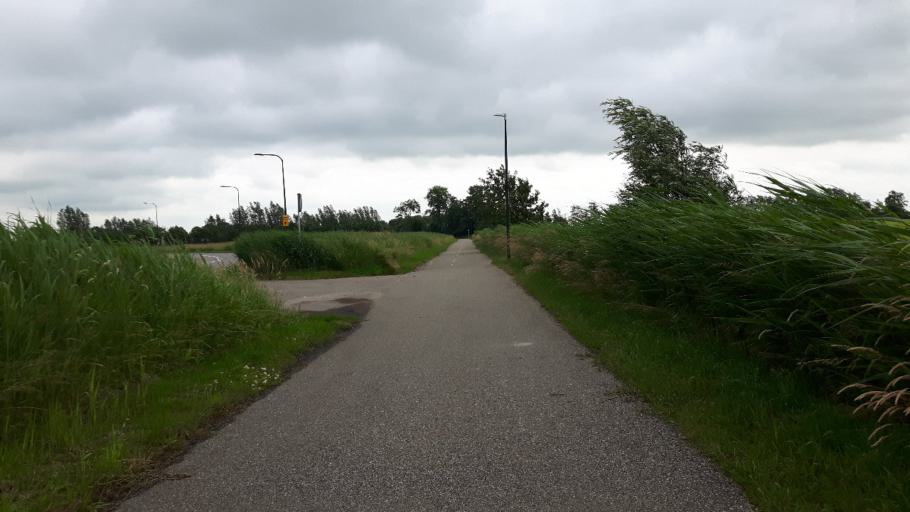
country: NL
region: Utrecht
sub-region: Gemeente Oudewater
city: Oudewater
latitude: 52.0581
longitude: 4.8417
